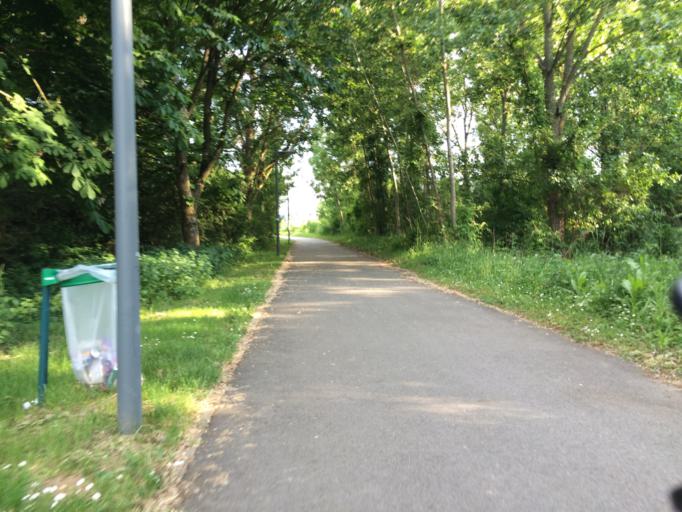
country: FR
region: Ile-de-France
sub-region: Departement de l'Essonne
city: Lisses
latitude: 48.5998
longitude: 2.4368
